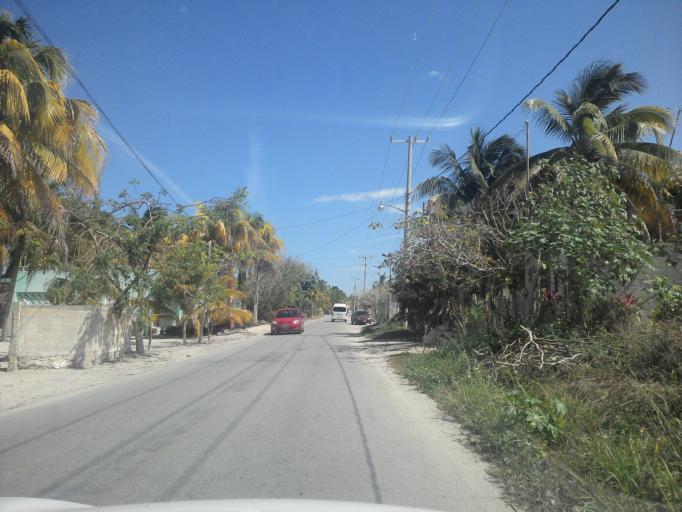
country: MX
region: Yucatan
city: Telchac Puerto
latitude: 21.3414
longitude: -89.2757
